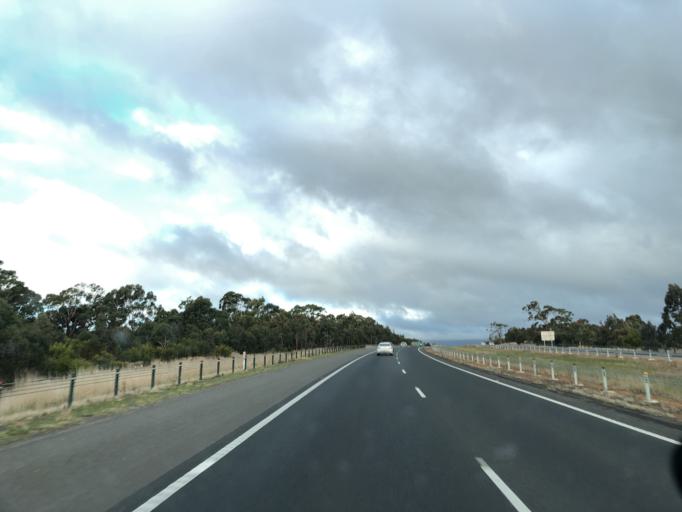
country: AU
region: Victoria
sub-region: Mount Alexander
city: Castlemaine
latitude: -37.2736
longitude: 144.4827
